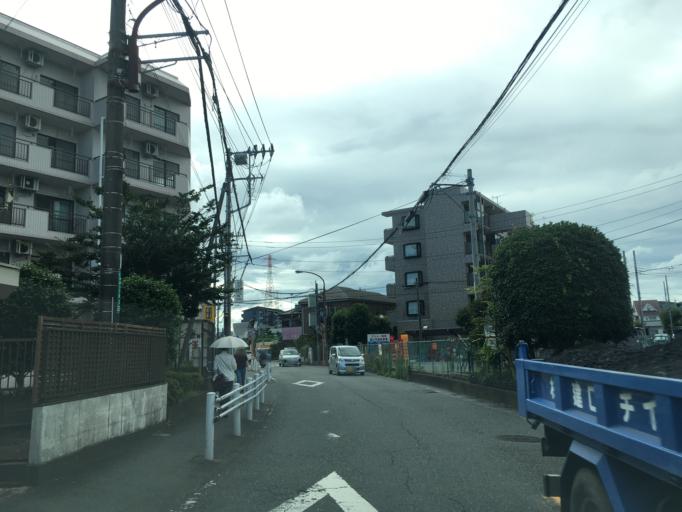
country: JP
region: Tokyo
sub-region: Machida-shi
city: Machida
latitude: 35.5568
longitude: 139.4166
